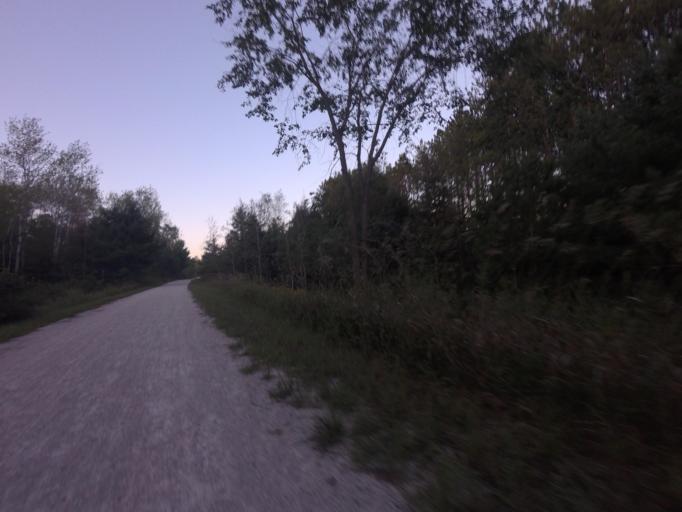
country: CA
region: Ontario
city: Orangeville
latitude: 43.9423
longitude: -79.8405
